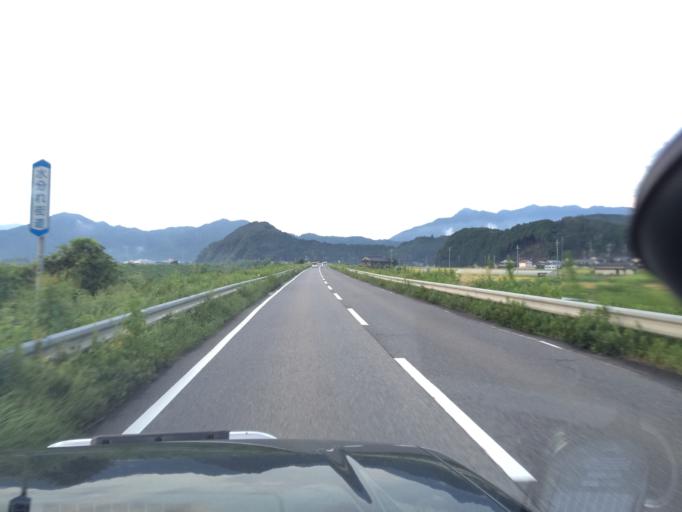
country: JP
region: Hyogo
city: Nishiwaki
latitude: 35.1440
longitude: 135.0310
